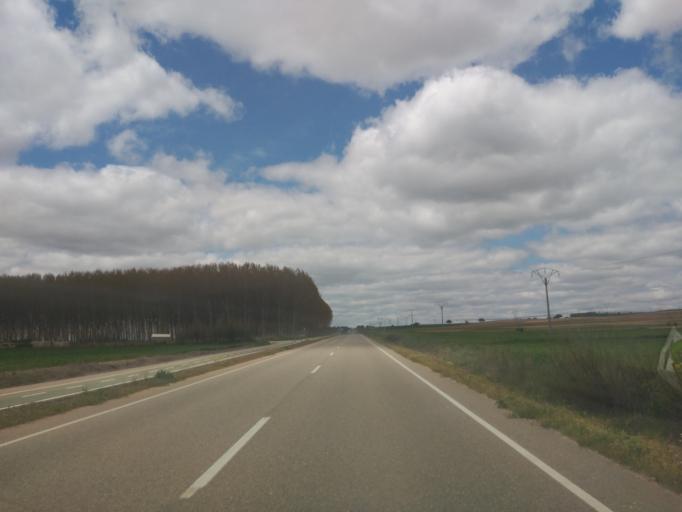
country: ES
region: Castille and Leon
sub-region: Provincia de Salamanca
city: Villamayor
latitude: 41.0234
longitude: -5.7222
